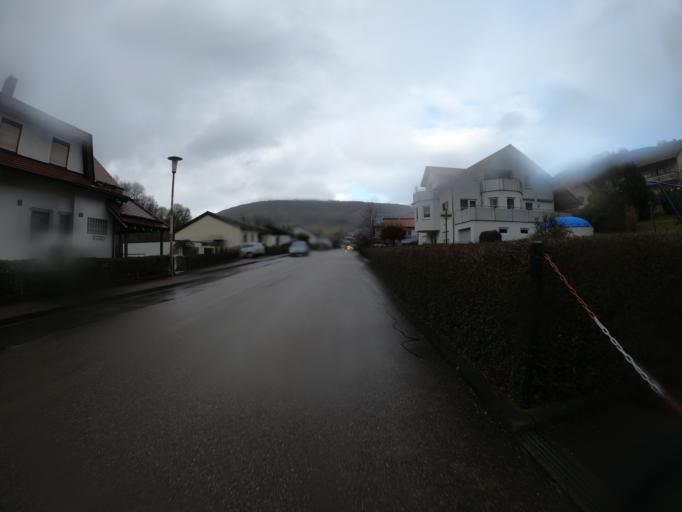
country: DE
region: Baden-Wuerttemberg
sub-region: Regierungsbezirk Stuttgart
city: Donzdorf
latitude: 48.7135
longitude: 9.8605
